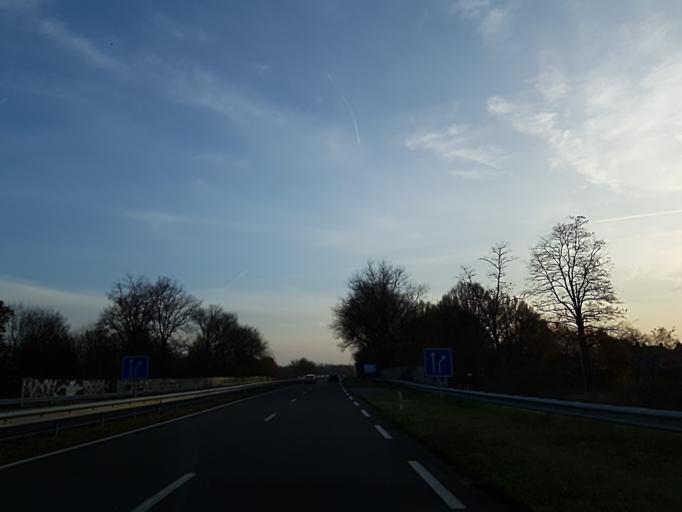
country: NL
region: North Brabant
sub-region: Roosendaal
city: Roosendaal
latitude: 51.5179
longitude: 4.4665
